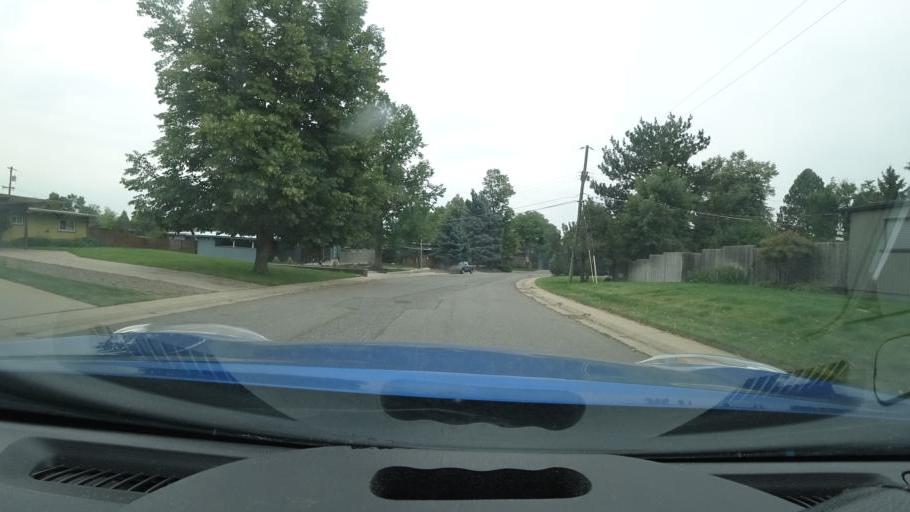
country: US
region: Colorado
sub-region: Arapahoe County
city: Glendale
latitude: 39.6839
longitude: -104.9210
